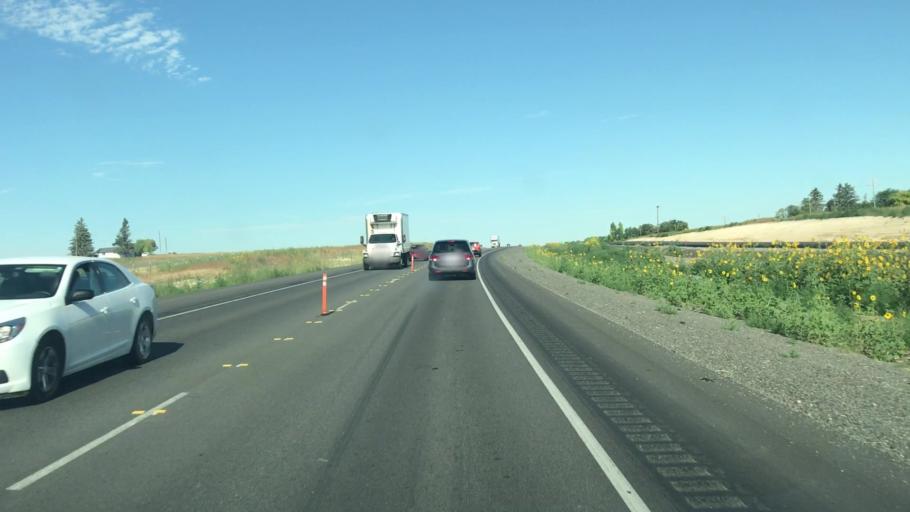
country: US
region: Idaho
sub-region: Twin Falls County
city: Hansen
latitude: 42.5752
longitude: -114.1052
